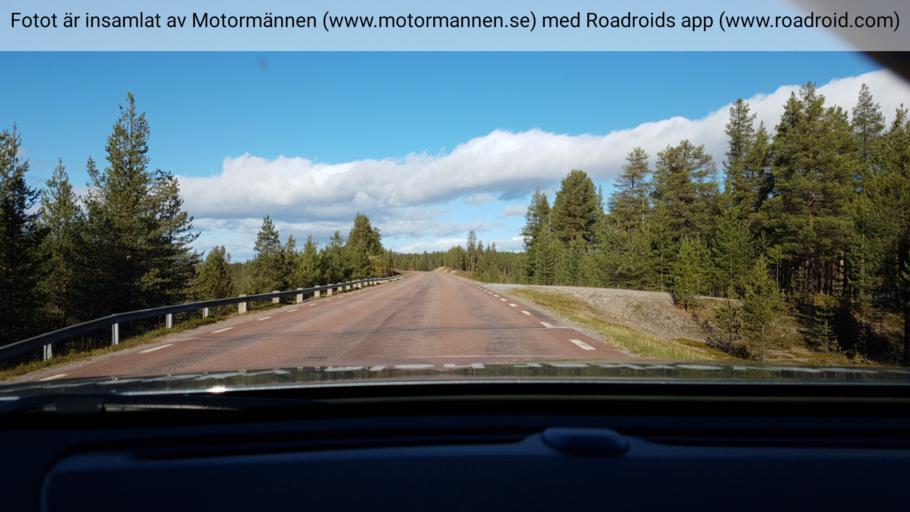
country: SE
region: Norrbotten
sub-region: Arjeplogs Kommun
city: Arjeplog
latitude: 66.0294
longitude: 18.0612
